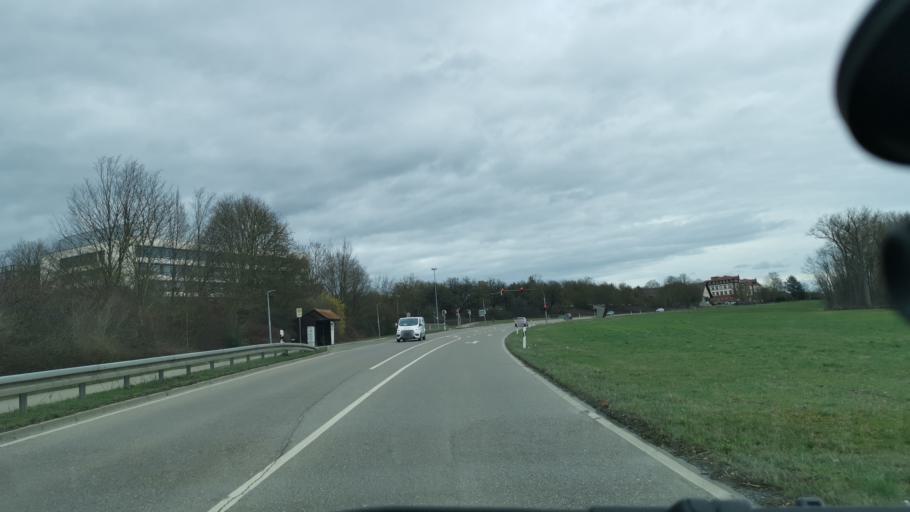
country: DE
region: Baden-Wuerttemberg
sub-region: Regierungsbezirk Stuttgart
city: Tamm
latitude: 48.9064
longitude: 9.1052
